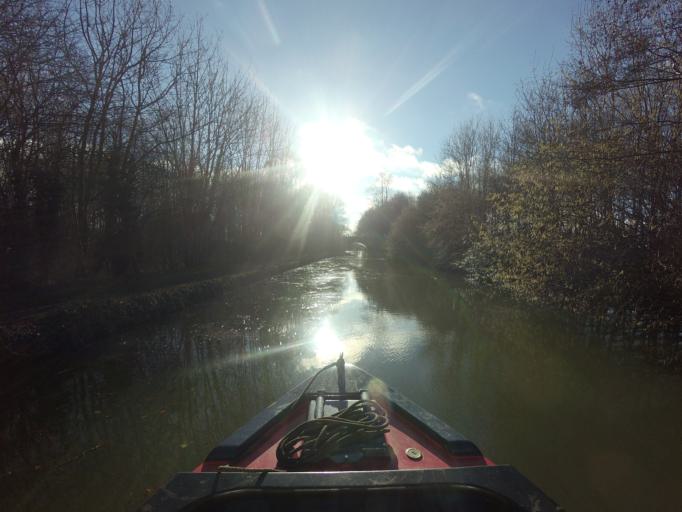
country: GB
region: England
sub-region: Northamptonshire
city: Long Buckby
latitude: 52.2593
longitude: -1.0853
